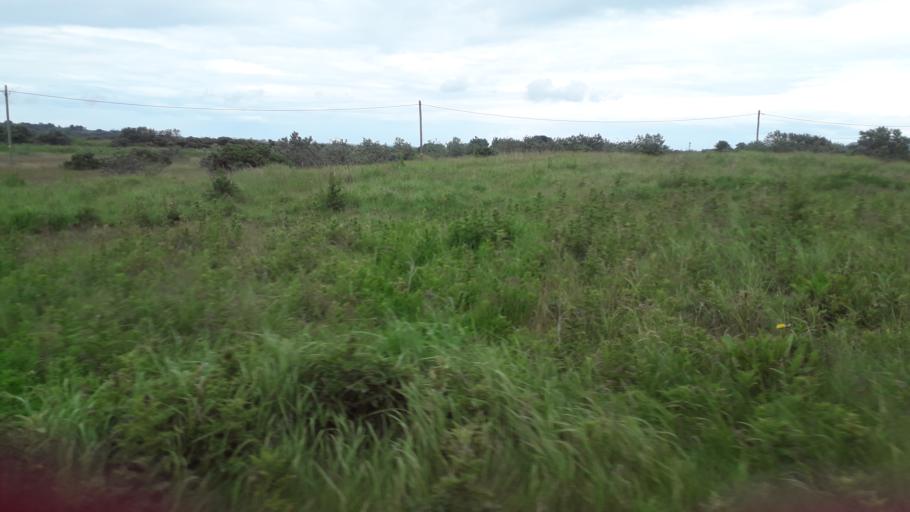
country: IE
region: Leinster
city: Dollymount
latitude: 53.3569
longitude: -6.1744
